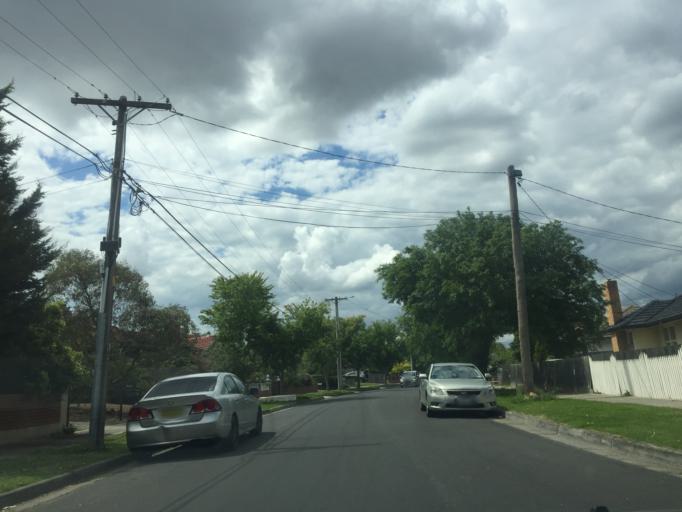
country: AU
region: Victoria
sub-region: Darebin
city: Kingsbury
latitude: -37.7155
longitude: 145.0195
